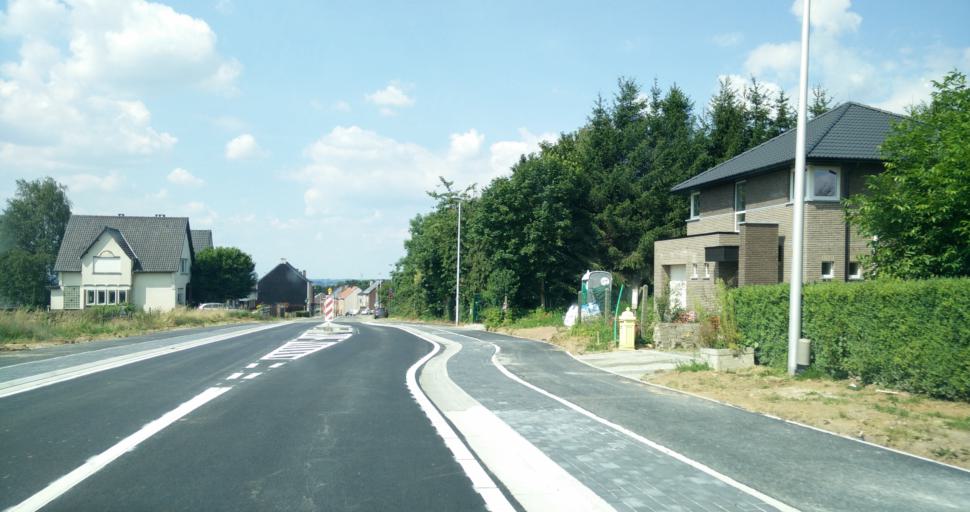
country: BE
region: Flanders
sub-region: Provincie Vlaams-Brabant
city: Halle
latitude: 50.7104
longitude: 4.2583
